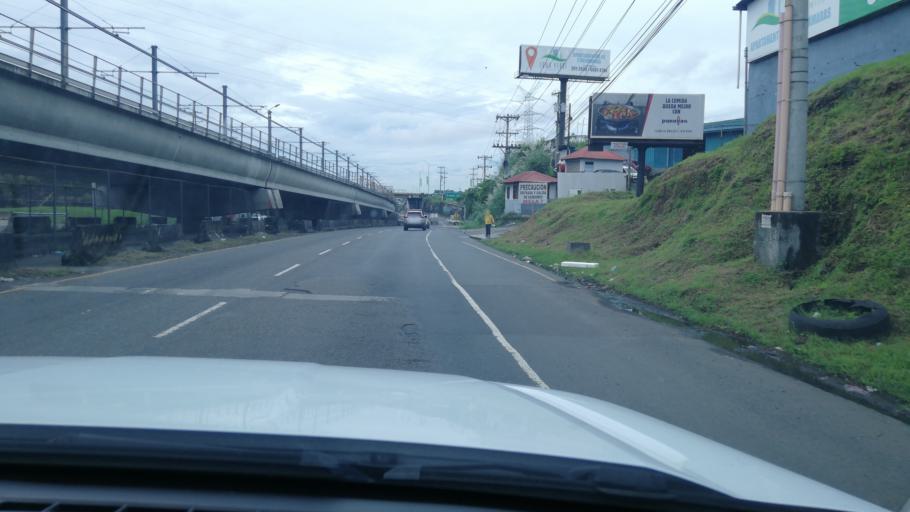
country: PA
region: Panama
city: Las Cumbres
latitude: 9.0615
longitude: -79.5101
